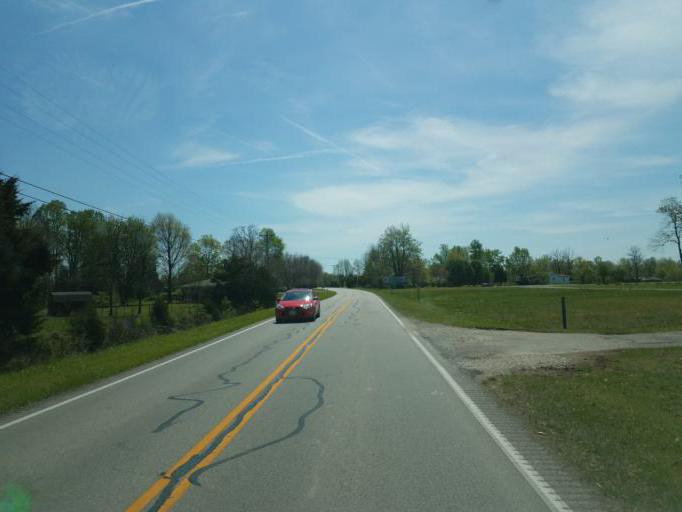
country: US
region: Kentucky
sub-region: Barren County
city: Cave City
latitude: 37.1357
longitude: -86.0377
